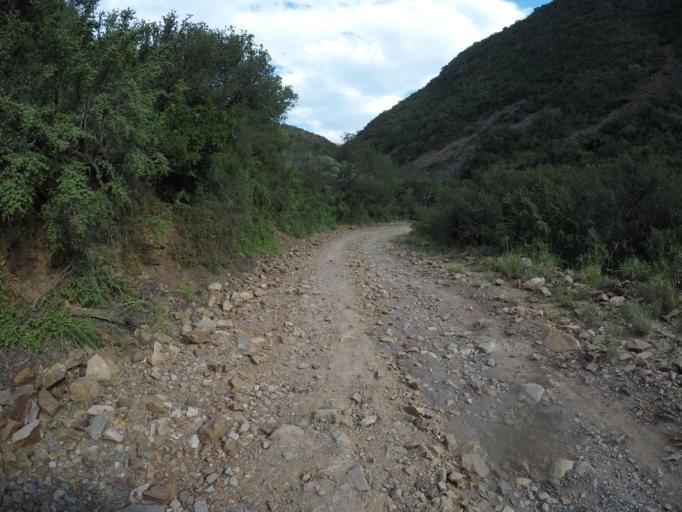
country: ZA
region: Eastern Cape
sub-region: Cacadu District Municipality
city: Kareedouw
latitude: -33.6502
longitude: 24.3361
